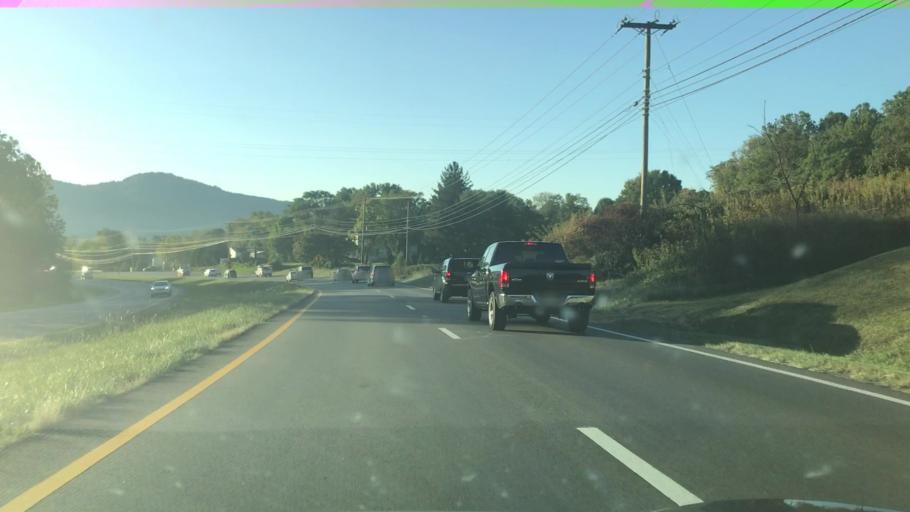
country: US
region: Virginia
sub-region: Botetourt County
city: Cloverdale
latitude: 37.3450
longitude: -79.8819
